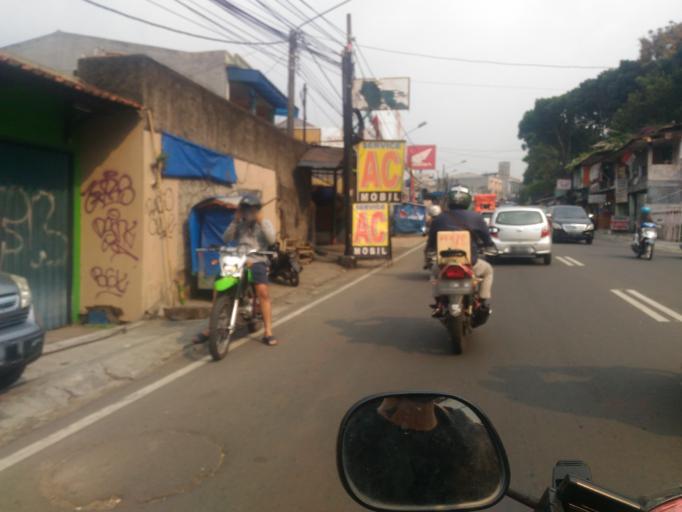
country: ID
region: West Java
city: Caringin
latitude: -6.6493
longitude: 106.8437
